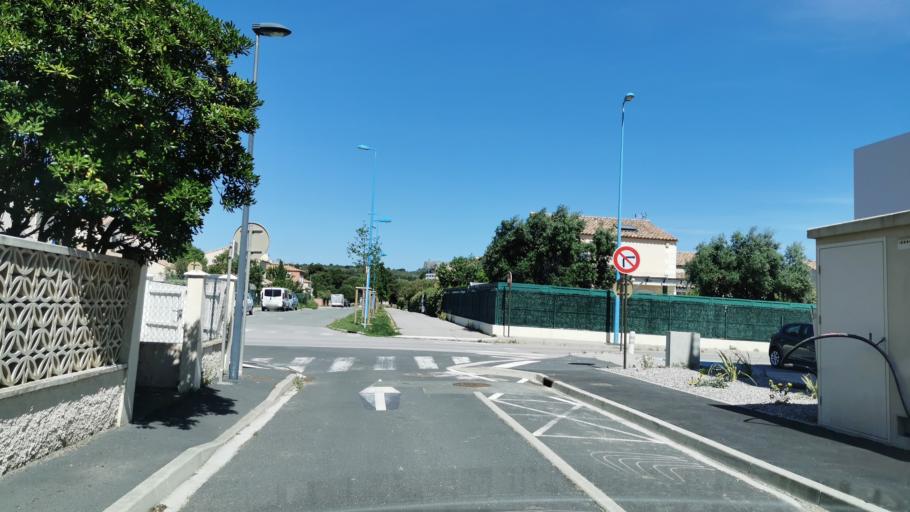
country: FR
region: Languedoc-Roussillon
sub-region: Departement de l'Aude
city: Armissan
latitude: 43.1577
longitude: 3.1631
